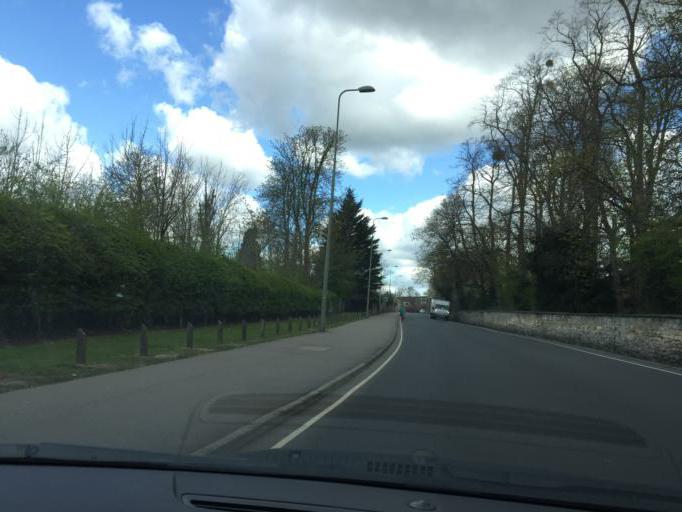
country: GB
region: England
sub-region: Oxfordshire
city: Oxford
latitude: 51.7534
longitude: -1.2363
